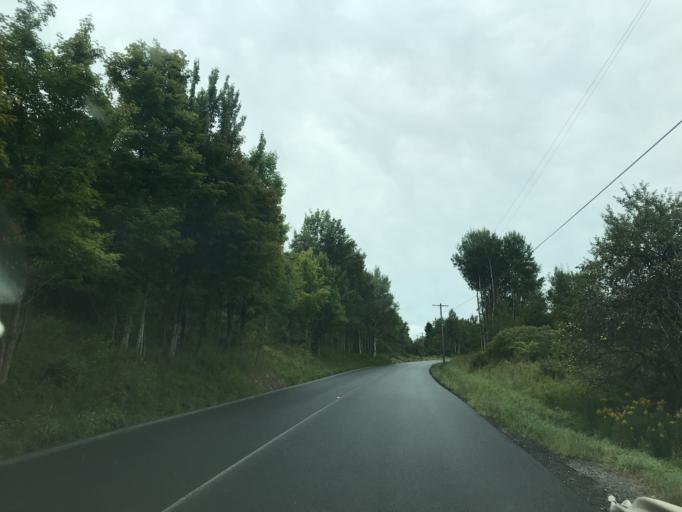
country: US
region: New York
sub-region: Delaware County
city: Stamford
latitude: 42.5222
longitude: -74.6221
